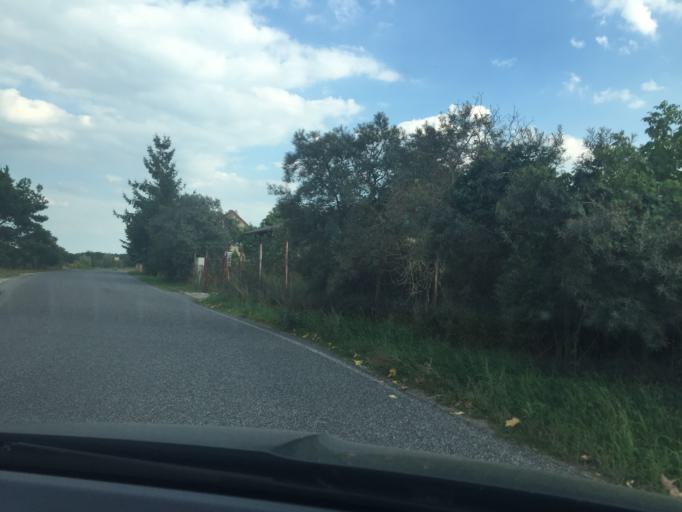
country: DE
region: Brandenburg
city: Spreenhagen
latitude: 52.3568
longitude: 13.8410
